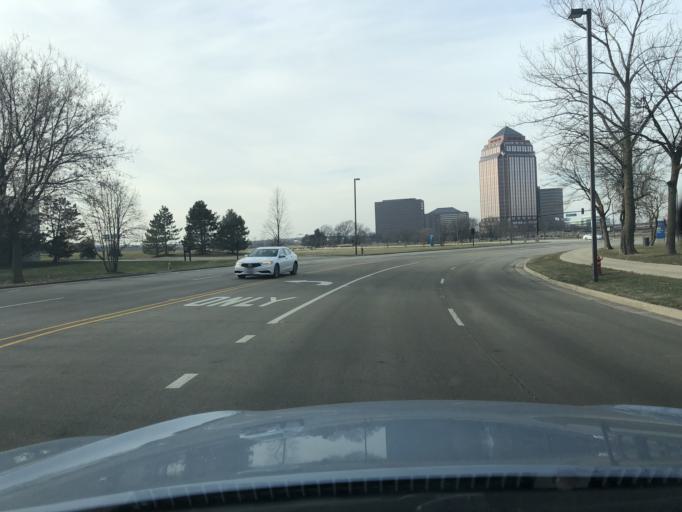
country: US
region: Illinois
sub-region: DuPage County
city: Itasca
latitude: 41.9857
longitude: -88.0081
